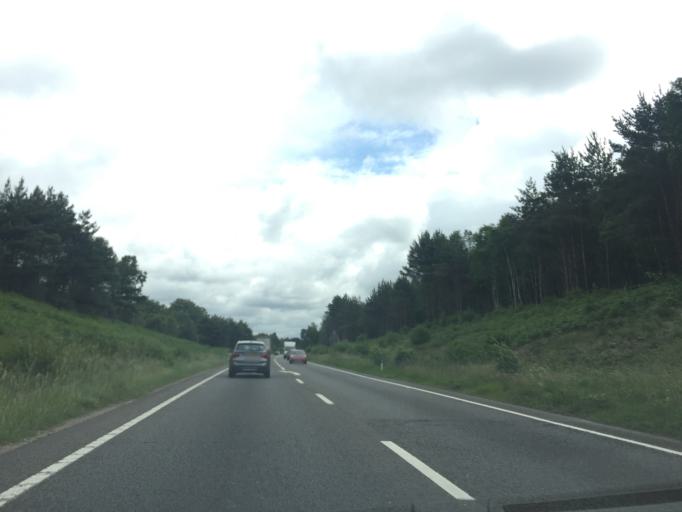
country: GB
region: England
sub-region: Dorset
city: Ferndown
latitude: 50.8080
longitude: -1.9329
